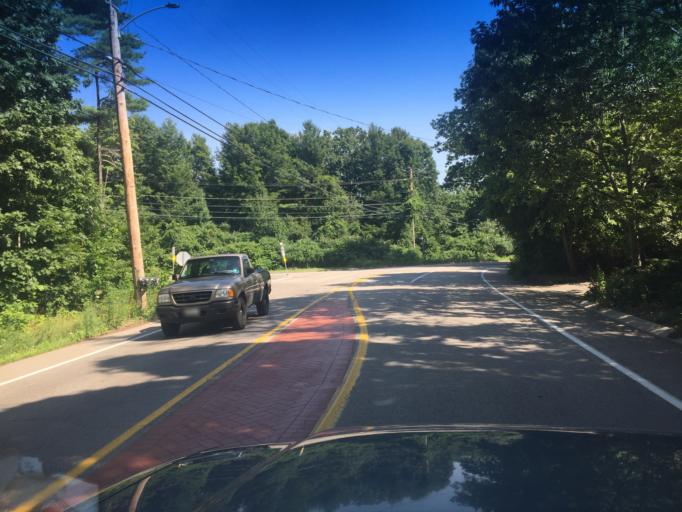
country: US
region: Maine
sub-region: York County
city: York Harbor
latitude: 43.1541
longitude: -70.6371
